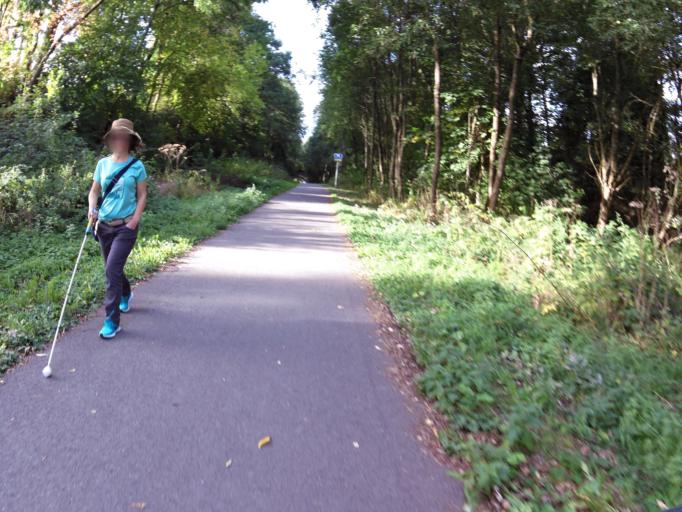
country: BE
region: Wallonia
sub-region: Province de Liege
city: Saint-Vith
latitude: 50.2775
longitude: 6.1320
